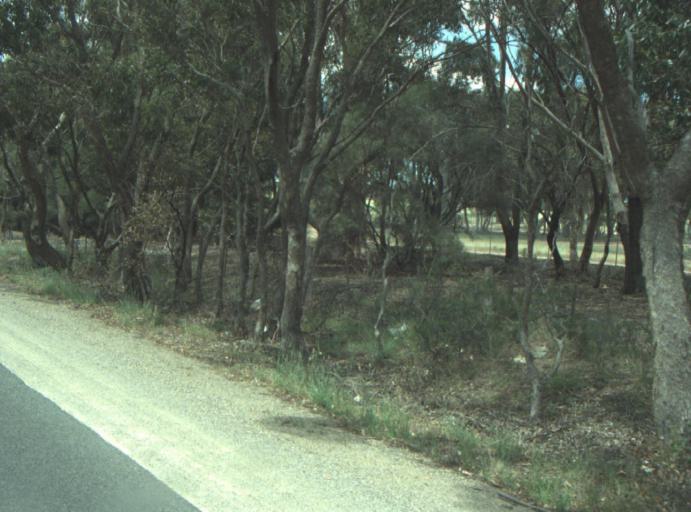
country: AU
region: Victoria
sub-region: Wyndham
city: Little River
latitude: -37.8774
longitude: 144.4143
